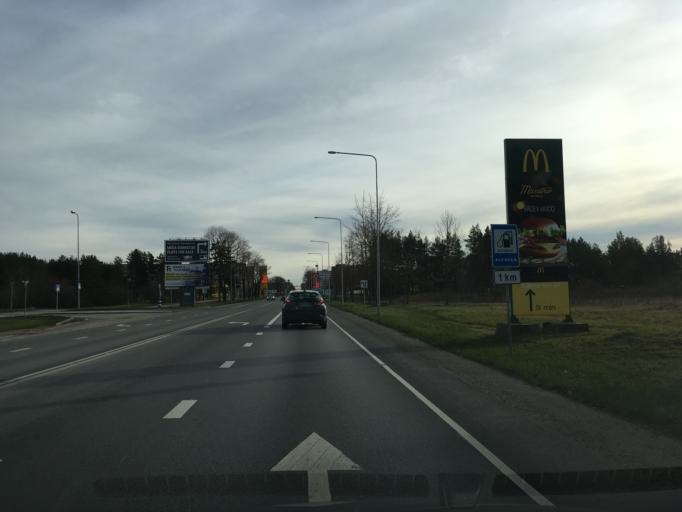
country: EE
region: Ida-Virumaa
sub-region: Narva linn
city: Narva
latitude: 59.3854
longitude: 28.1538
